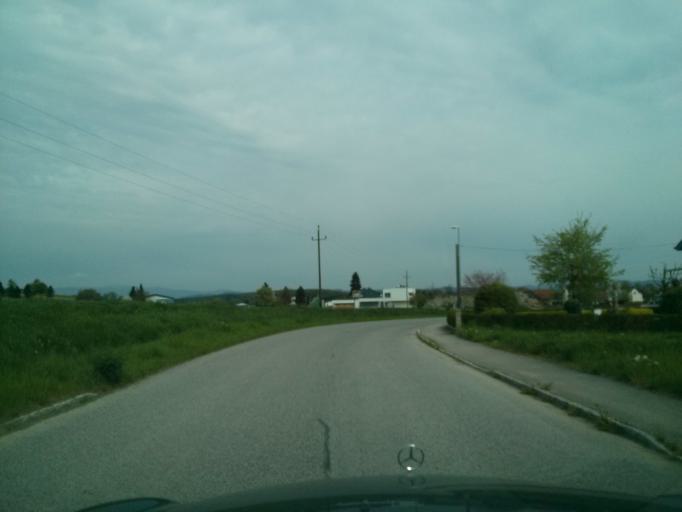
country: AT
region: Burgenland
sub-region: Politischer Bezirk Oberwart
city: Oberwart
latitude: 47.3132
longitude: 16.2042
